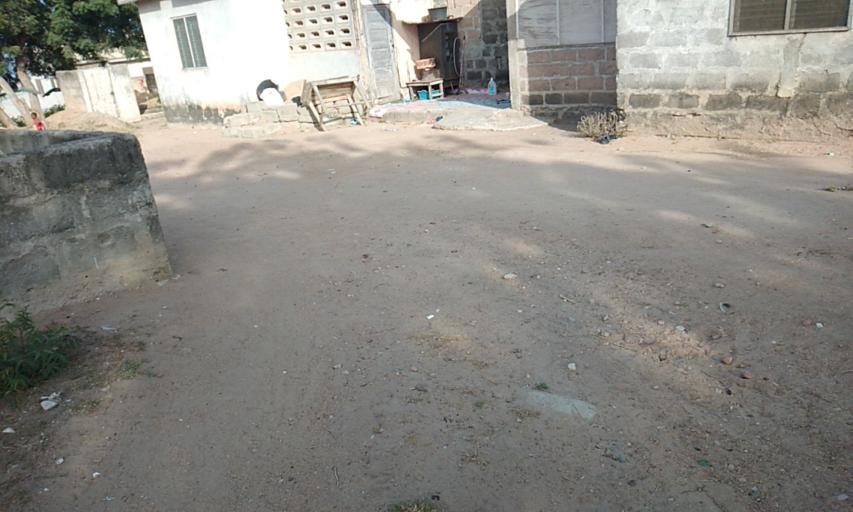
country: GH
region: Central
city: Winneba
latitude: 5.3551
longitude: -0.6152
